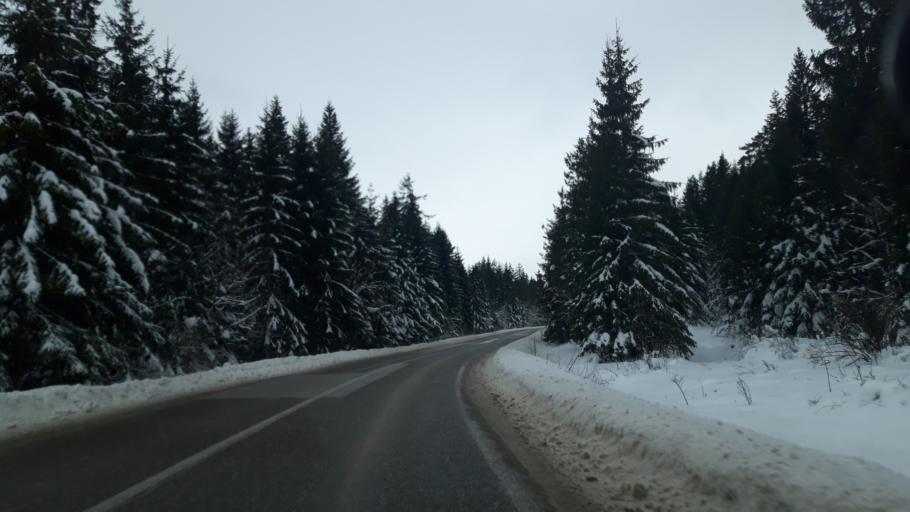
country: BA
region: Republika Srpska
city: Han Pijesak
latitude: 44.0525
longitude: 18.9348
